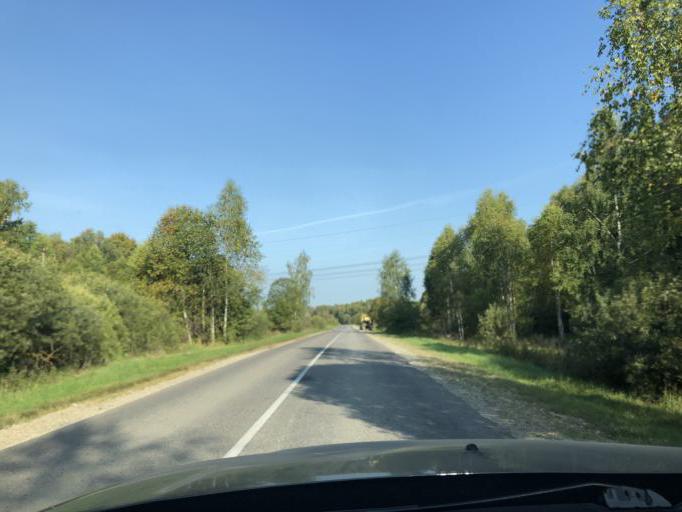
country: RU
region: Tula
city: Leninskiy
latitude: 54.3328
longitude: 37.3844
